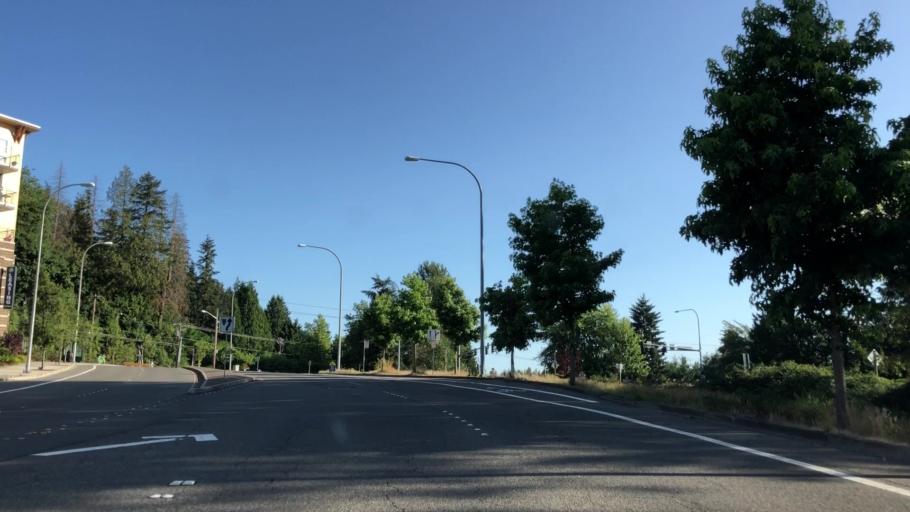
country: US
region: Washington
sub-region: King County
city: Bothell
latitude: 47.7671
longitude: -122.1910
